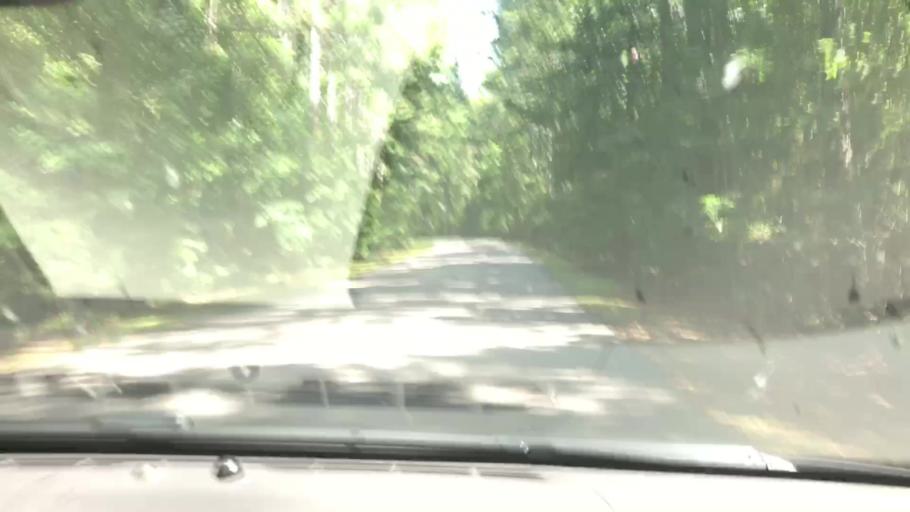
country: US
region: Georgia
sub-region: Troup County
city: La Grange
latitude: 33.0704
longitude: -85.1360
